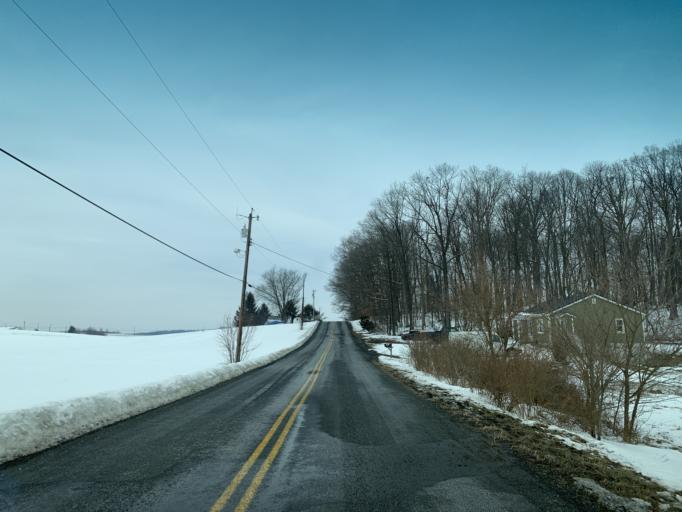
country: US
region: Pennsylvania
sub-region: York County
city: Susquehanna Trails
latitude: 39.7149
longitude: -76.4174
